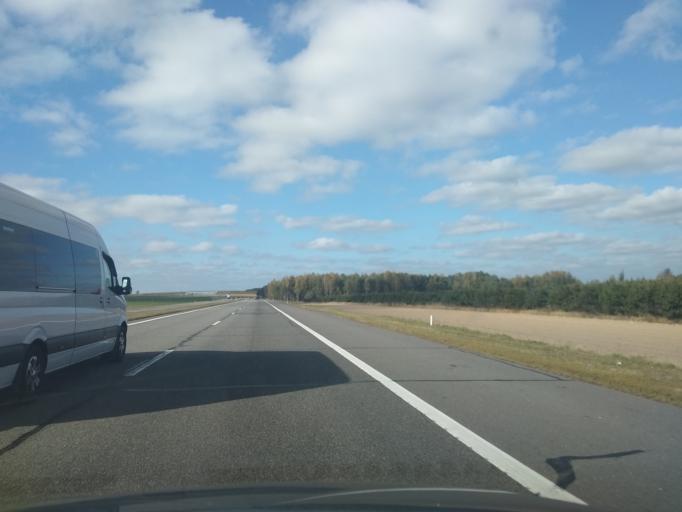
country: BY
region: Minsk
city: Stowbtsy
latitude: 53.5338
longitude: 26.8226
